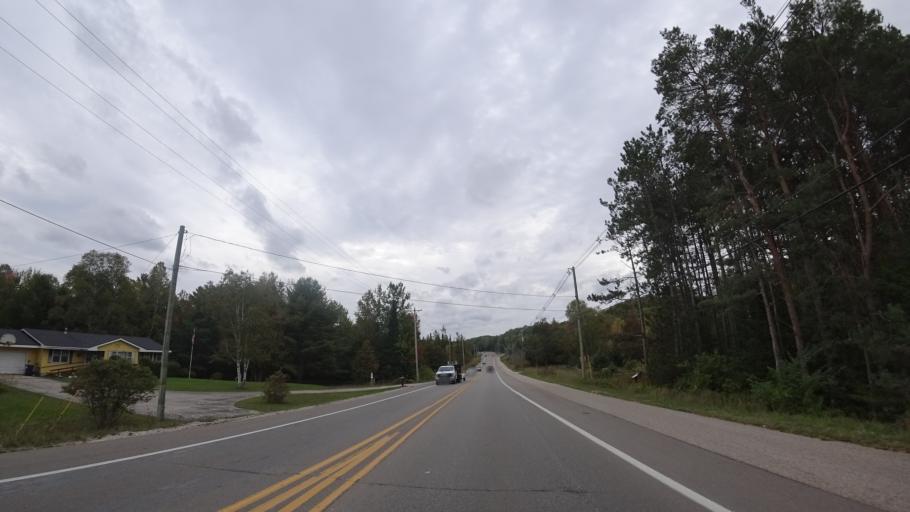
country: US
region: Michigan
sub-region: Emmet County
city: Petoskey
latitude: 45.4184
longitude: -84.9045
